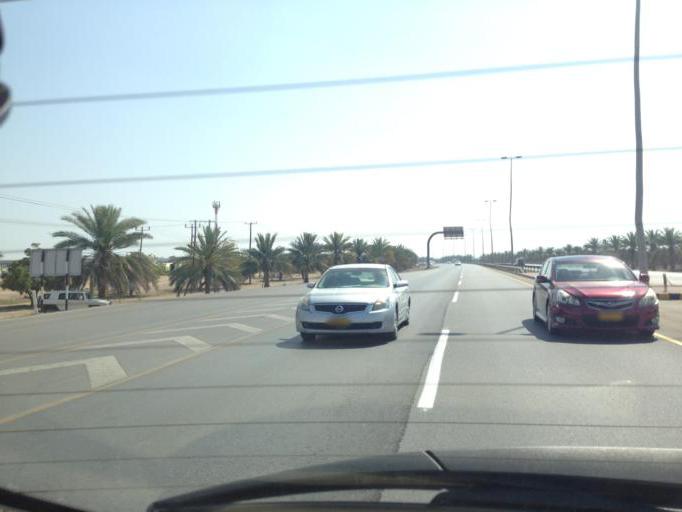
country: OM
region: Muhafazat Masqat
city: As Sib al Jadidah
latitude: 23.5899
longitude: 58.2192
